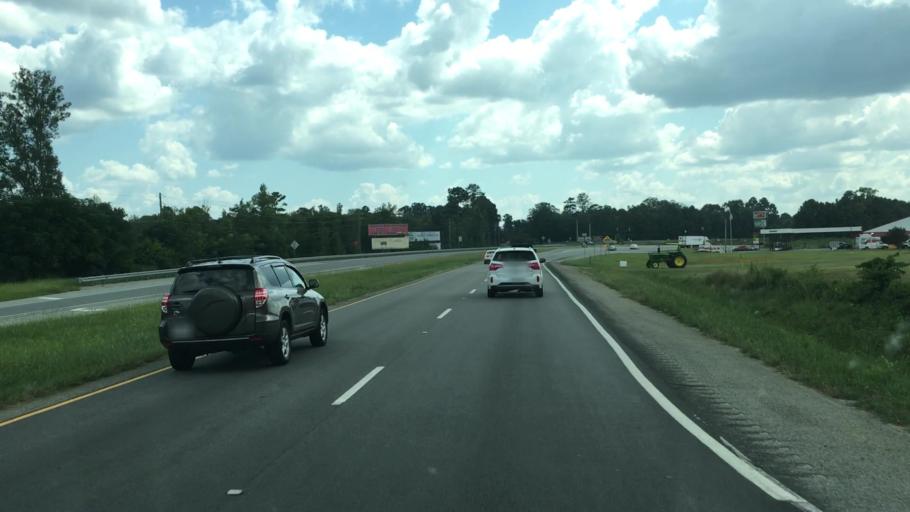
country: US
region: Georgia
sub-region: Putnam County
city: Eatonton
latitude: 33.3500
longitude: -83.3915
